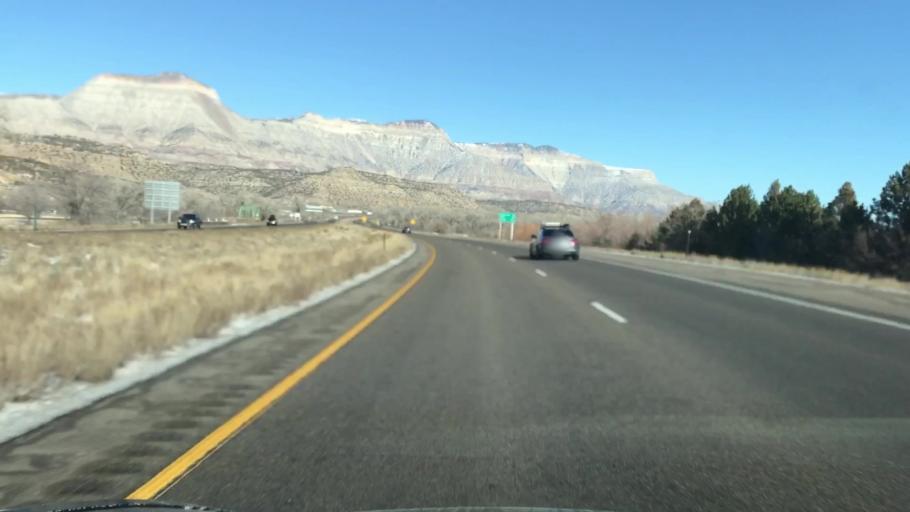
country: US
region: Colorado
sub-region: Garfield County
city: Parachute
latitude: 39.3337
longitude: -108.1947
